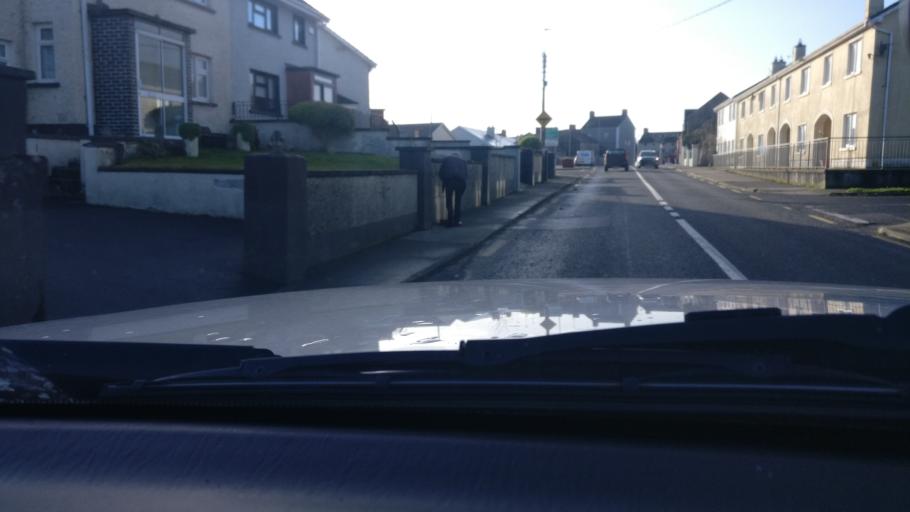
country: IE
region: Leinster
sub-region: An Longfort
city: Ballymahon
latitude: 53.5656
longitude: -7.7629
